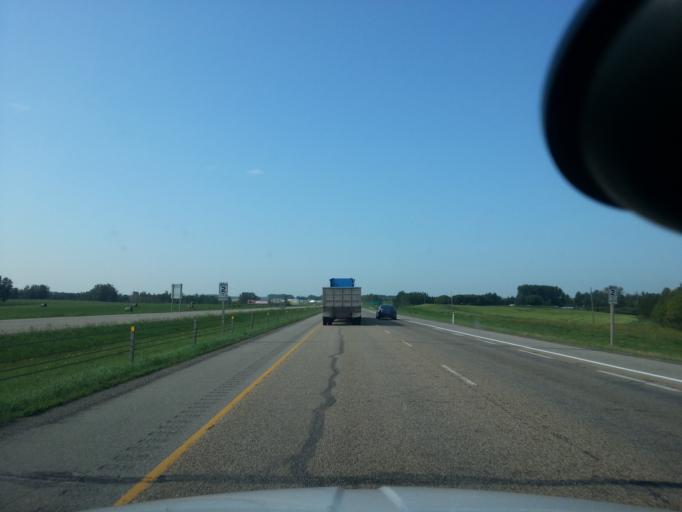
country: CA
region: Alberta
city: Penhold
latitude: 51.9945
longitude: -113.9740
